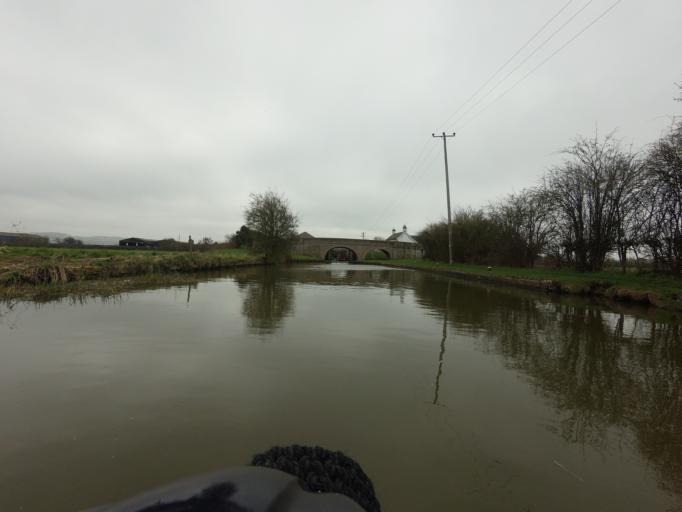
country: GB
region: England
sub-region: Buckinghamshire
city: Cheddington
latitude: 51.8674
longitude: -0.6486
